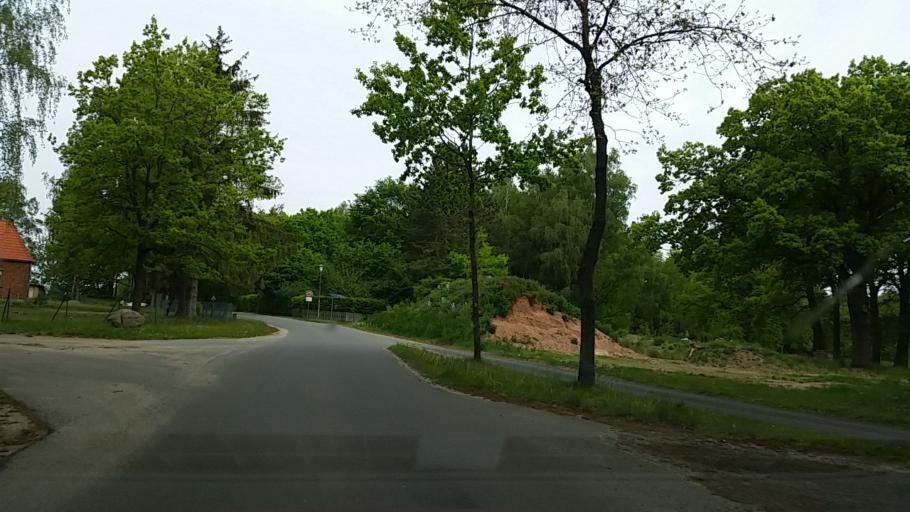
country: DE
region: Lower Saxony
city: Wieren
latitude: 52.8622
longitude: 10.6694
